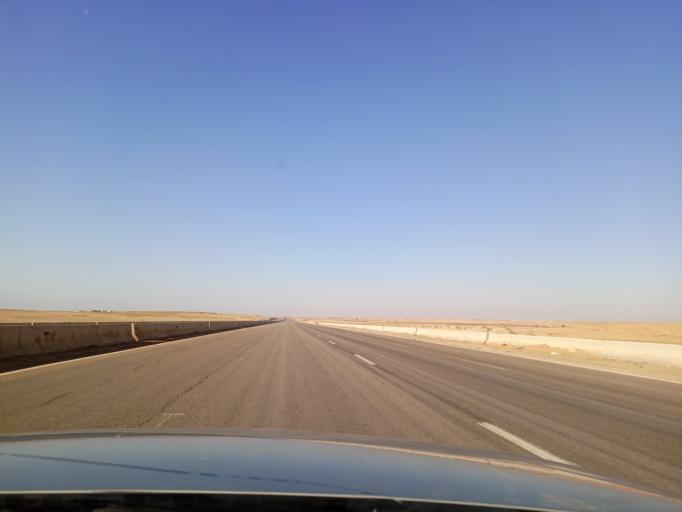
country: EG
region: Muhafazat al Fayyum
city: Tamiyah
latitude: 29.6114
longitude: 30.9205
